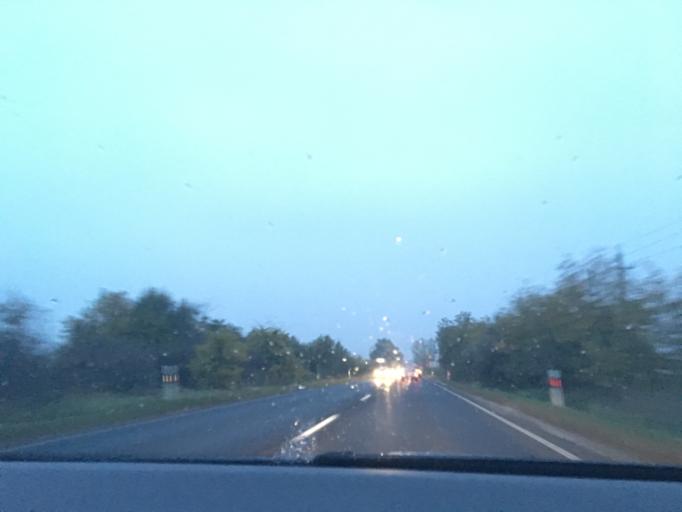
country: HU
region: Pest
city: Pilis
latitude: 47.2928
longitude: 19.5336
